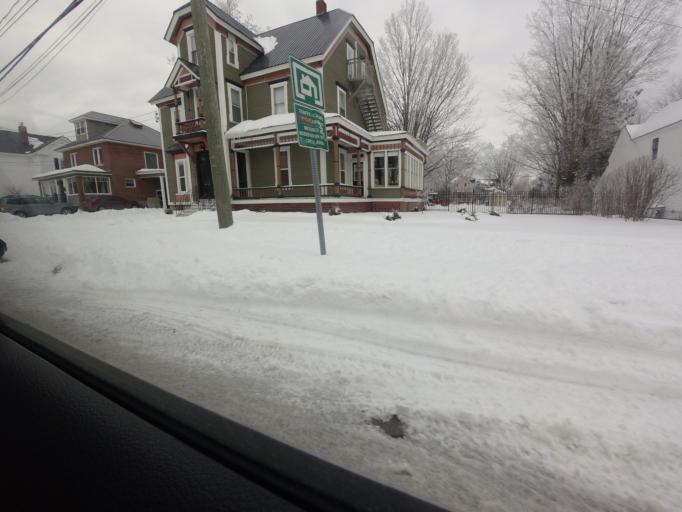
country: CA
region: New Brunswick
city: Fredericton
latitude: 45.9560
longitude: -66.6385
